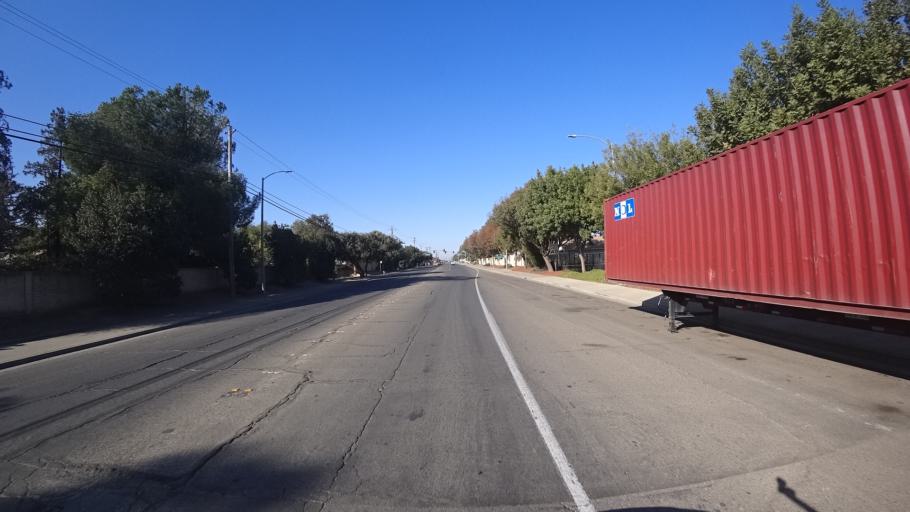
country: US
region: California
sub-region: Yolo County
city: Woodland
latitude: 38.6921
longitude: -121.7956
